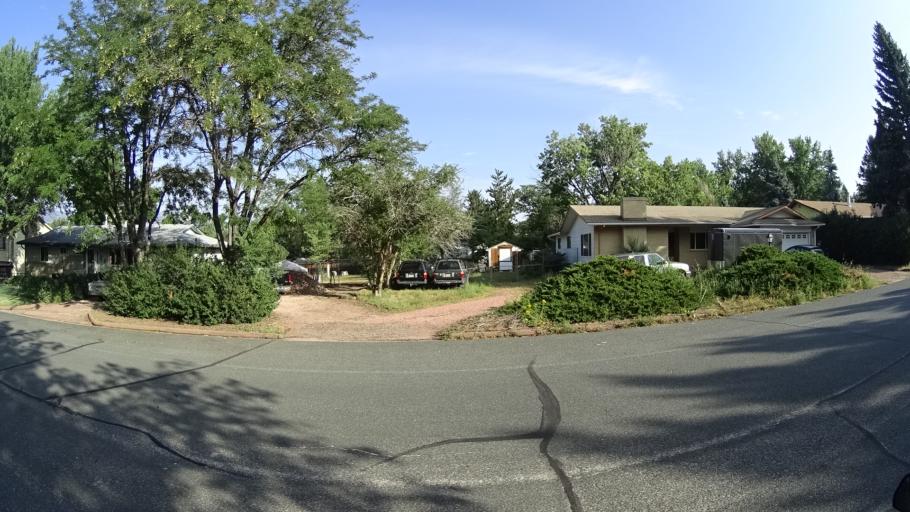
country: US
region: Colorado
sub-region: El Paso County
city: Colorado Springs
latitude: 38.8927
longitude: -104.8109
